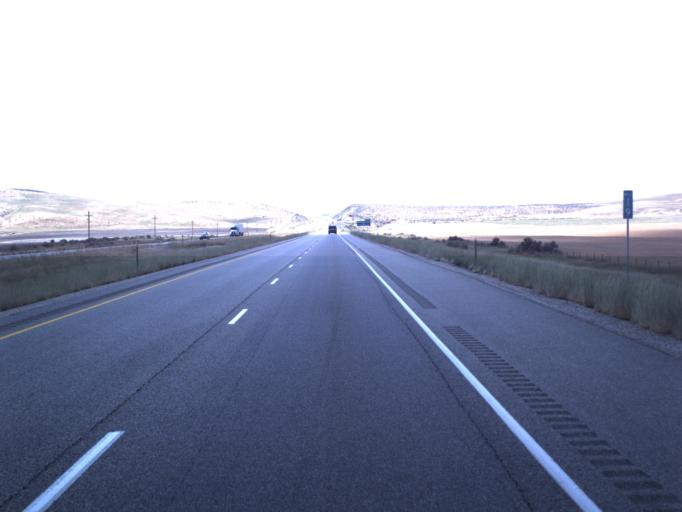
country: US
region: Utah
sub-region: Box Elder County
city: Garland
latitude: 41.8915
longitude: -112.5140
